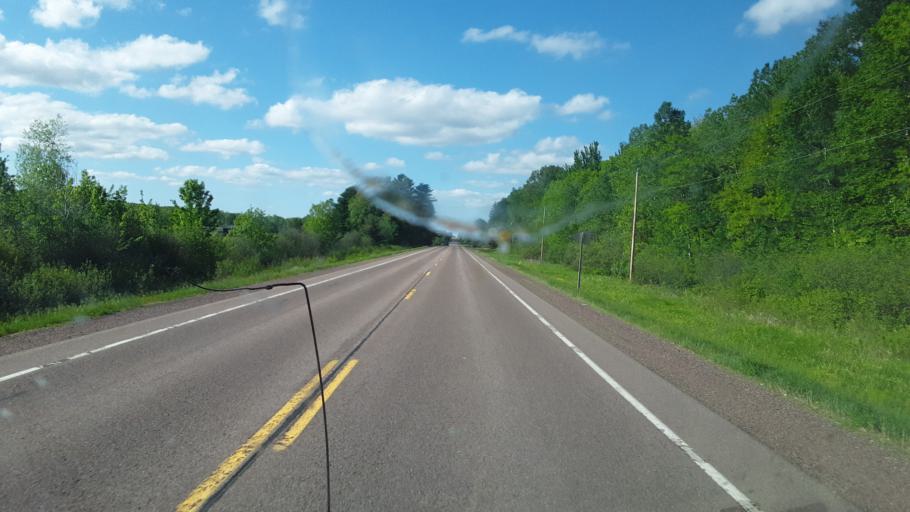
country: US
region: Wisconsin
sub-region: Wood County
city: Marshfield
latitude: 44.5199
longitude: -90.1799
